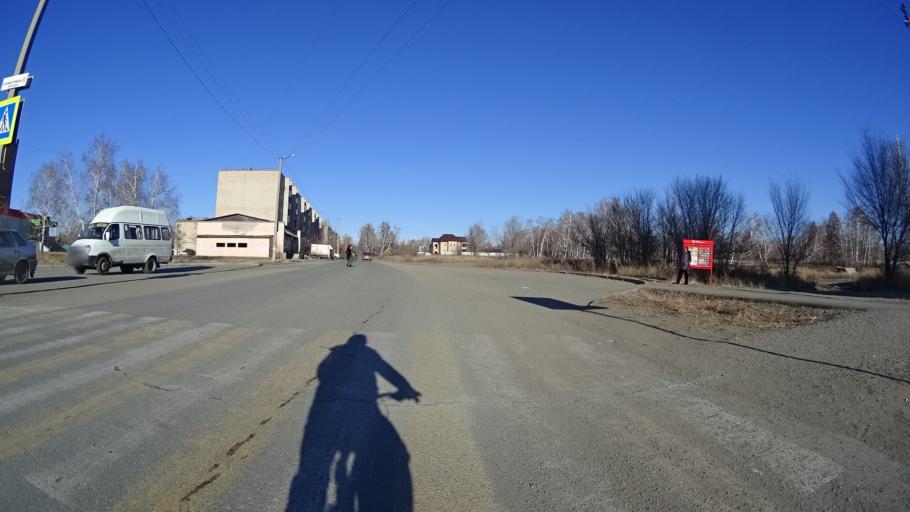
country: RU
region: Chelyabinsk
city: Troitsk
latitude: 54.0476
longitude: 61.6406
